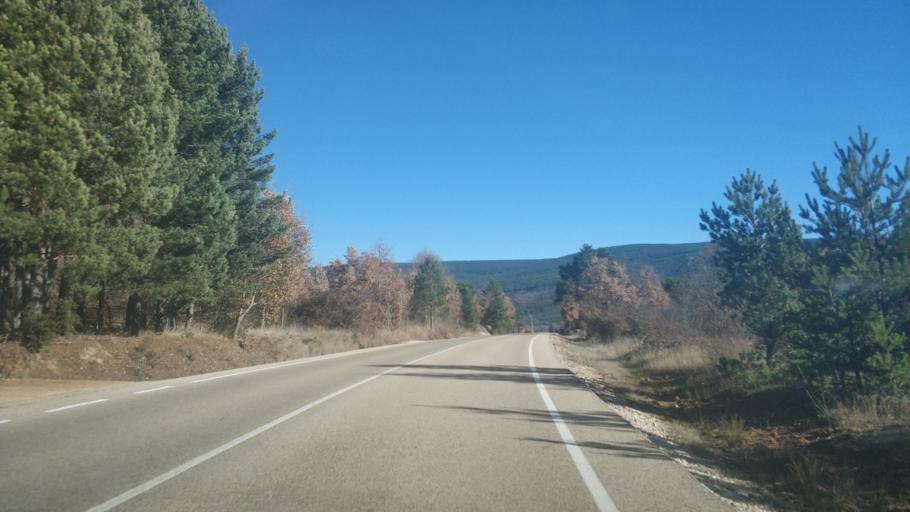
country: ES
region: Castille and Leon
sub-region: Provincia de Soria
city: Vinuesa
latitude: 41.9002
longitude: -2.7695
